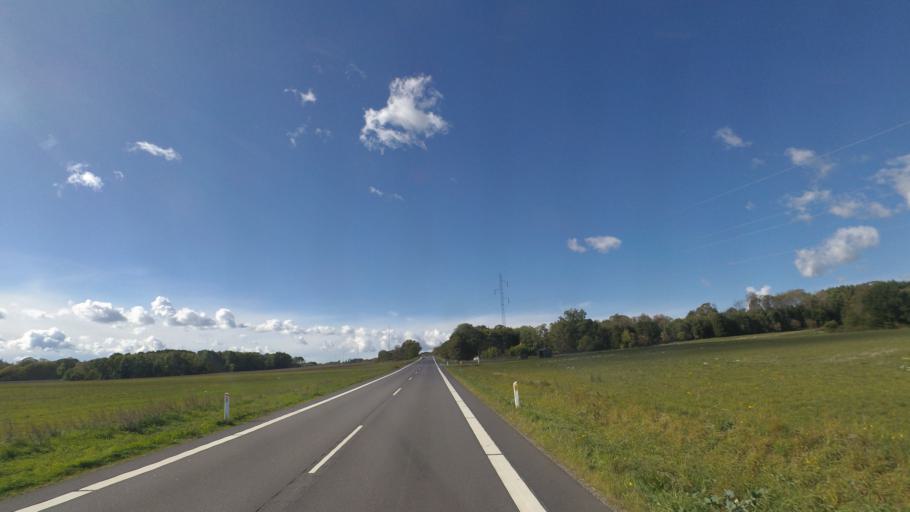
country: DK
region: Capital Region
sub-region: Bornholm Kommune
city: Nexo
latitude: 55.0614
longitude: 15.0405
